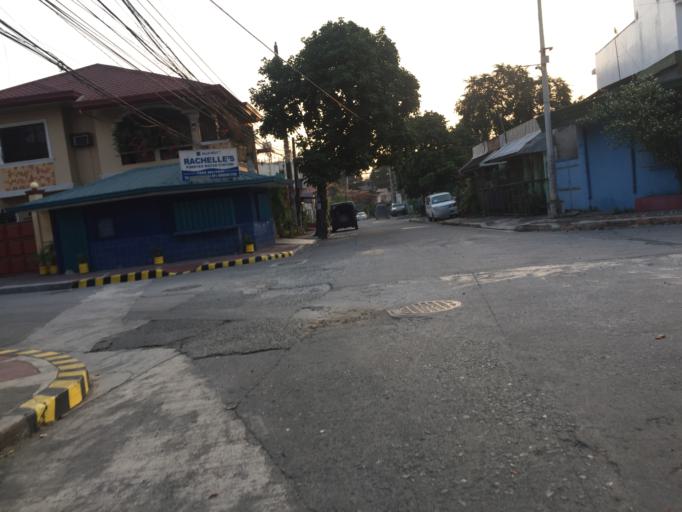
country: PH
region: Calabarzon
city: Bagong Pagasa
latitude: 14.6749
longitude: 121.0229
